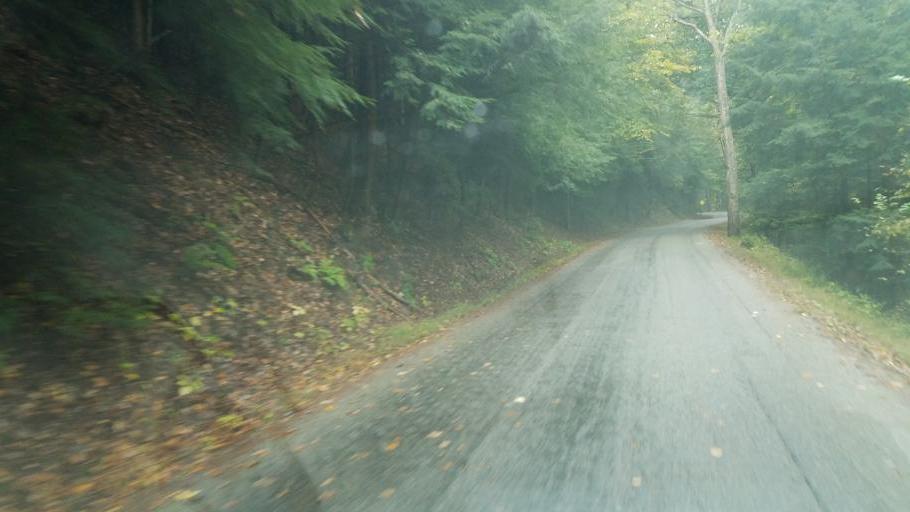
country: US
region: Ohio
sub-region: Ashland County
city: Loudonville
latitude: 40.6157
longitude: -82.3152
